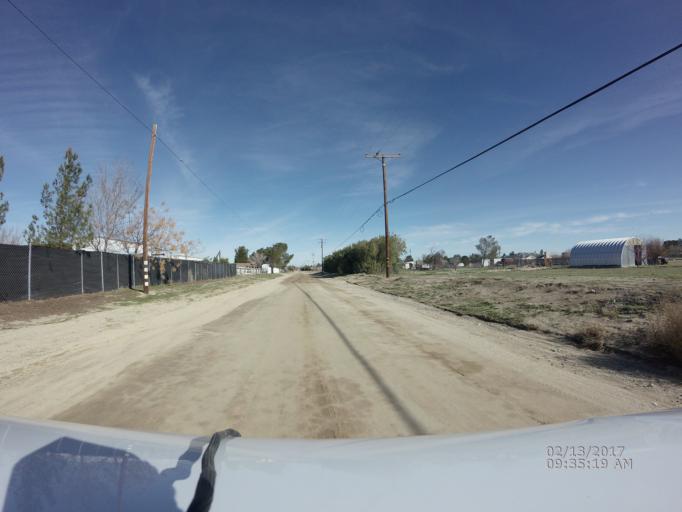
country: US
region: California
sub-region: Los Angeles County
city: Littlerock
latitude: 34.5308
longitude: -117.9669
